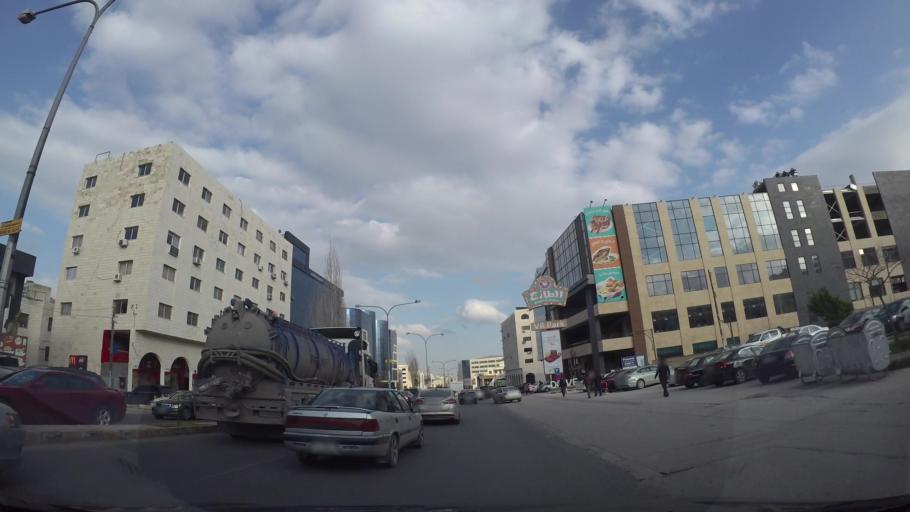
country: JO
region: Amman
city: Al Jubayhah
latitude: 31.9843
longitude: 35.8861
